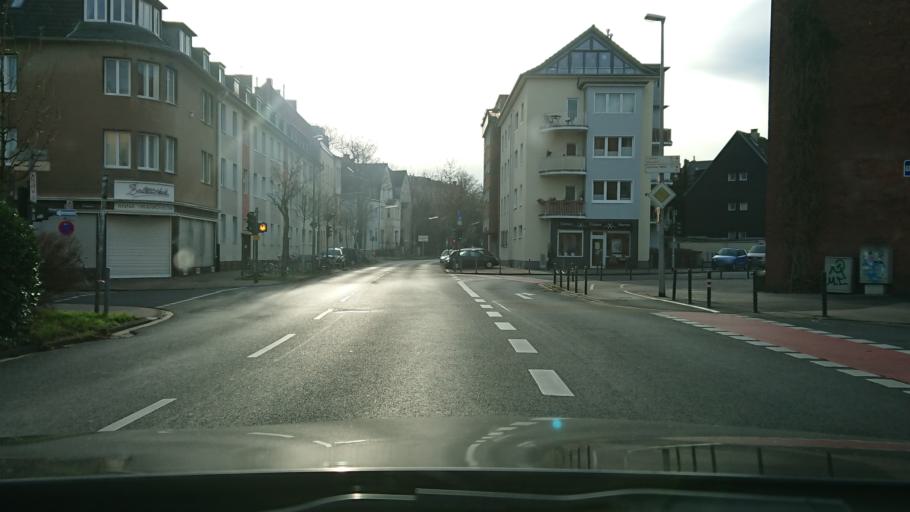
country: DE
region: North Rhine-Westphalia
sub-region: Regierungsbezirk Koln
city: Neustadt/Sued
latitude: 50.9293
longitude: 6.9197
